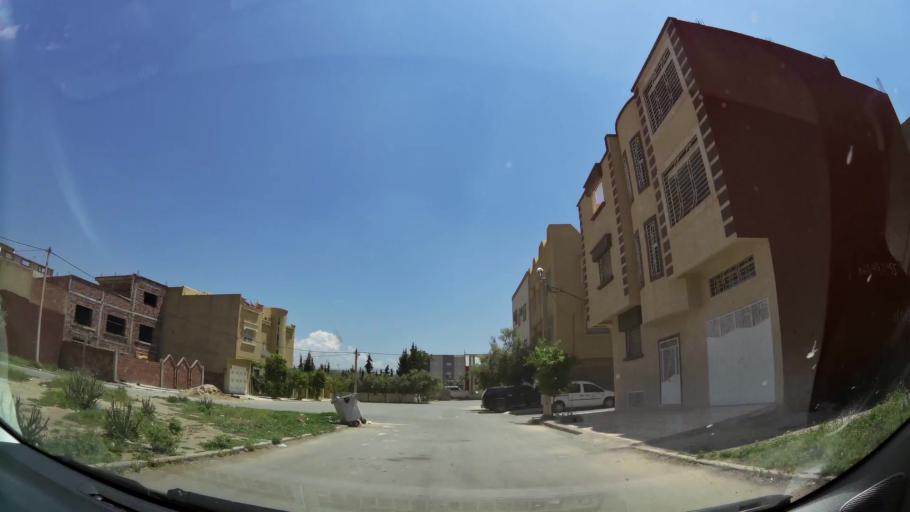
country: MA
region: Oriental
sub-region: Oujda-Angad
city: Oujda
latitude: 34.6631
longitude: -1.9487
